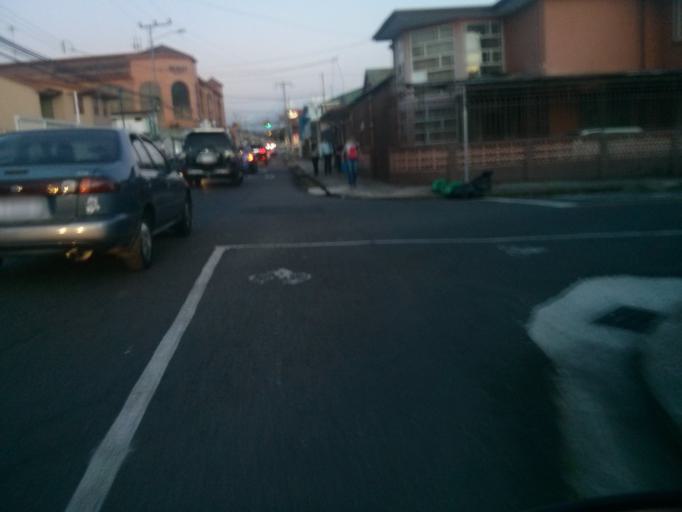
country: CR
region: San Jose
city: San Pedro
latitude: 9.9317
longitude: -84.0539
